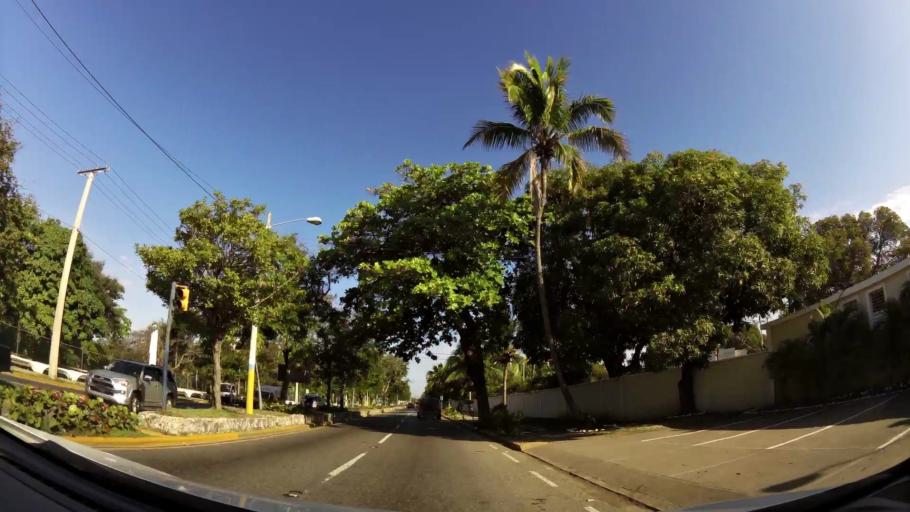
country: DO
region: Nacional
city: Ciudad Nueva
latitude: 18.4723
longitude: -69.8759
